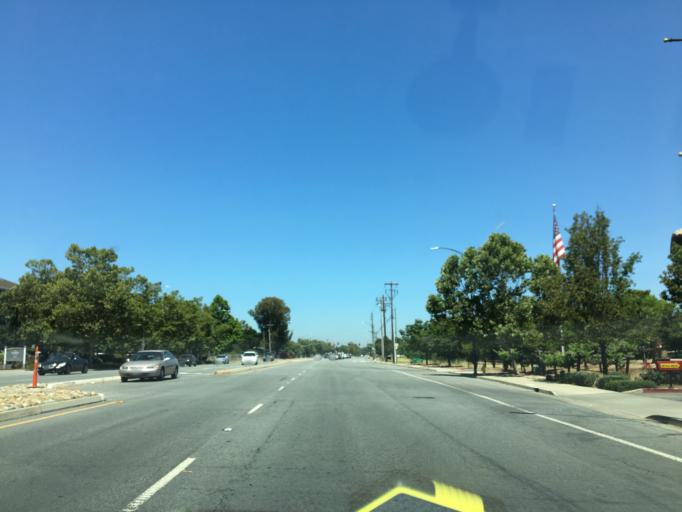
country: US
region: California
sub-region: Santa Clara County
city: Seven Trees
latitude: 37.3007
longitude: -121.7727
